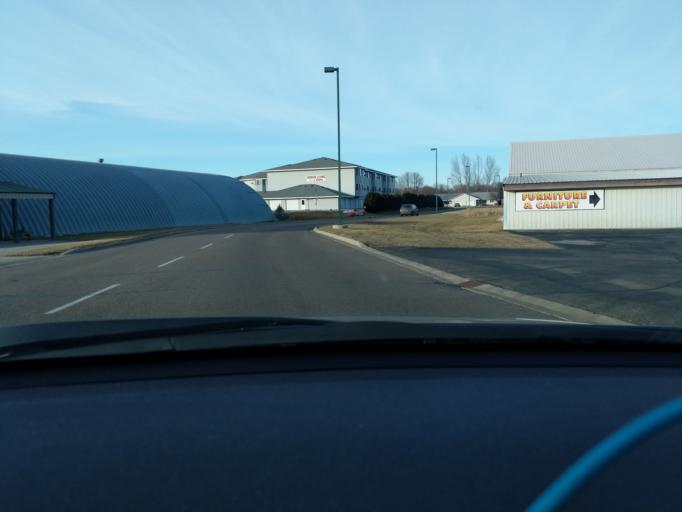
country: US
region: Minnesota
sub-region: Kandiyohi County
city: Willmar
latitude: 45.0945
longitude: -95.0448
